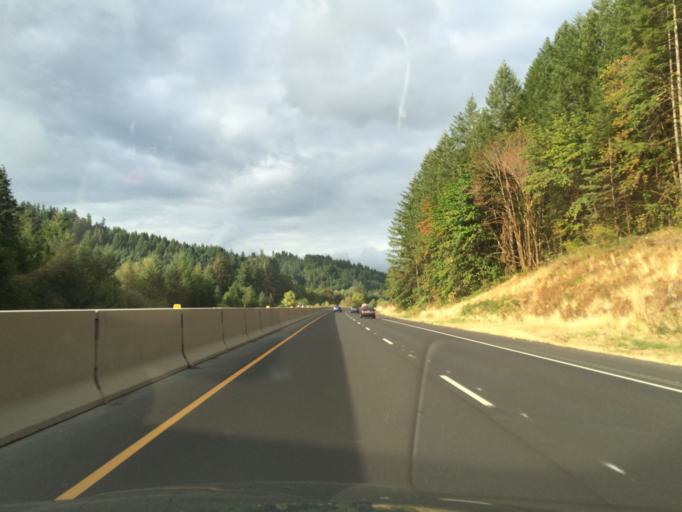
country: US
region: Oregon
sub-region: Douglas County
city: Drain
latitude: 43.7311
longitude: -123.1996
